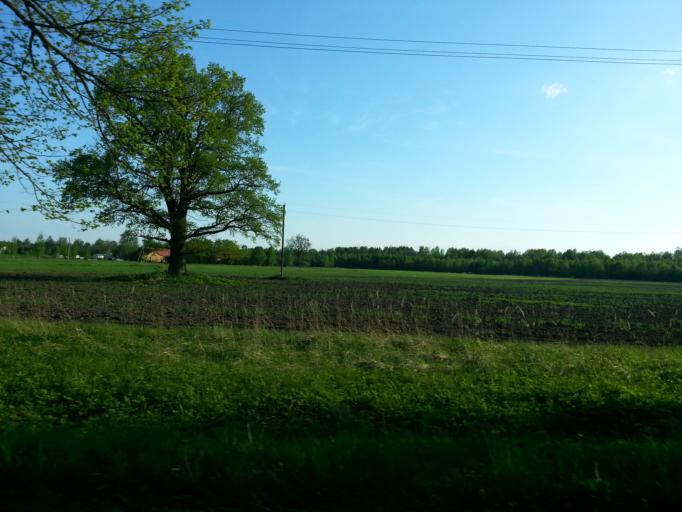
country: LT
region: Vilnius County
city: Ukmerge
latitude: 55.4228
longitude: 24.5631
